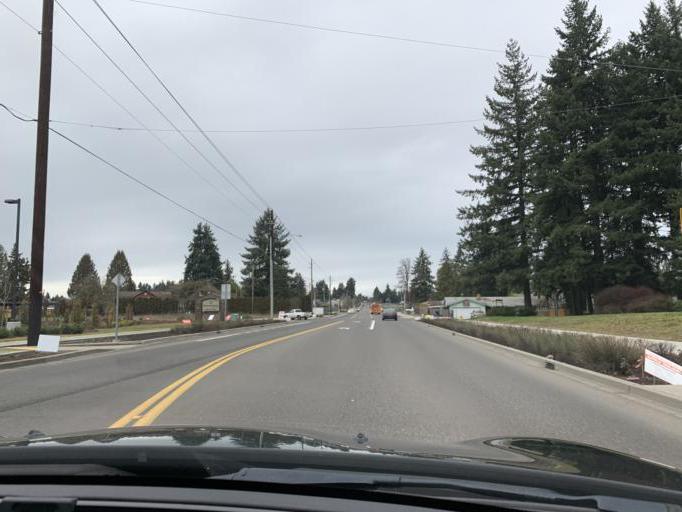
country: US
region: Washington
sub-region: Clark County
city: Five Corners
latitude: 45.6837
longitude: -122.5759
